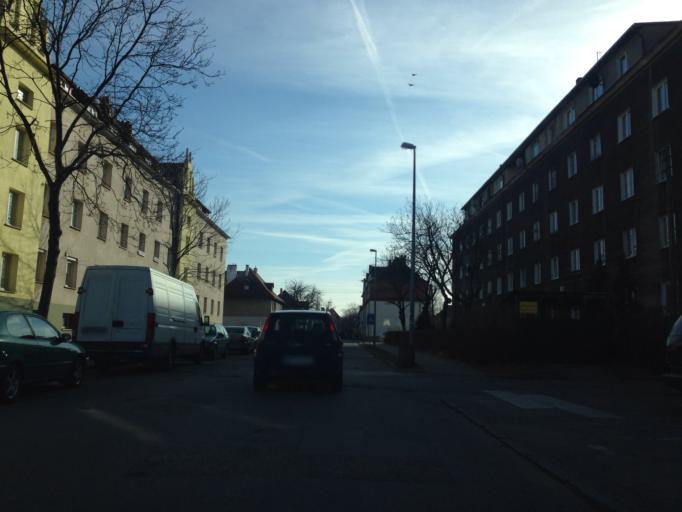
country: PL
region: Pomeranian Voivodeship
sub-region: Gdansk
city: Gdansk
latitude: 54.3871
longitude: 18.6285
